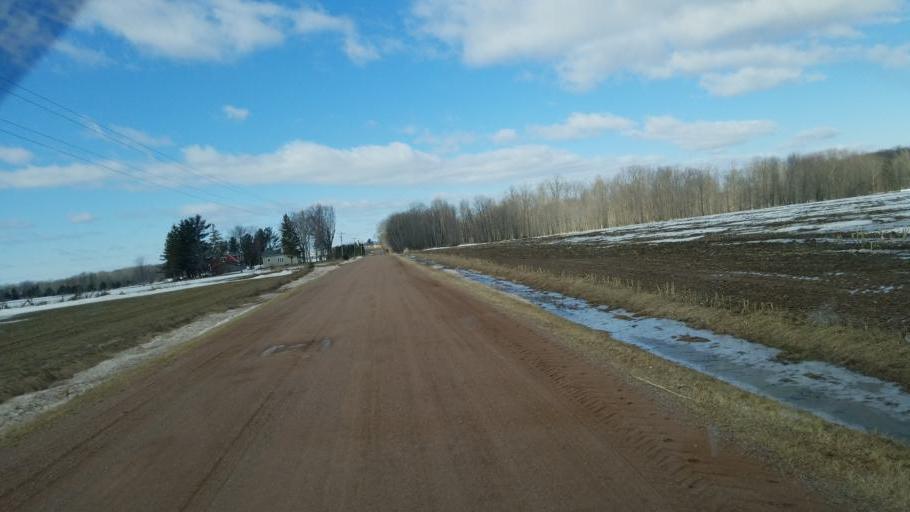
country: US
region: Wisconsin
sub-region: Clark County
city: Loyal
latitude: 44.6835
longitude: -90.4390
